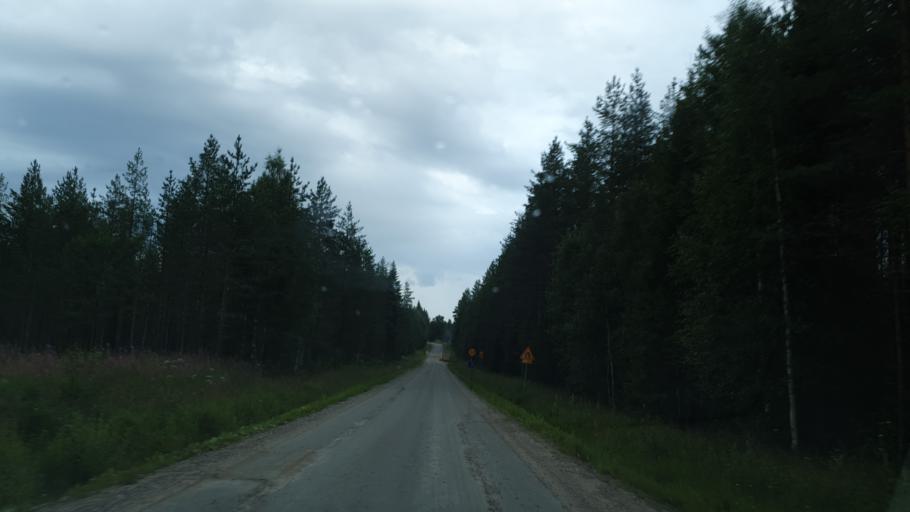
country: FI
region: Kainuu
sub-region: Kehys-Kainuu
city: Kuhmo
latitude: 64.2102
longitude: 29.3700
